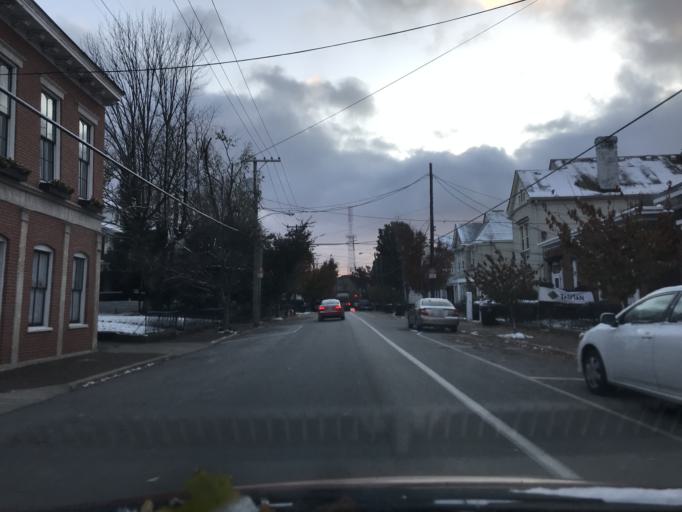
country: US
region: Indiana
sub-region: Clark County
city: Jeffersonville
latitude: 38.2600
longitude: -85.7201
